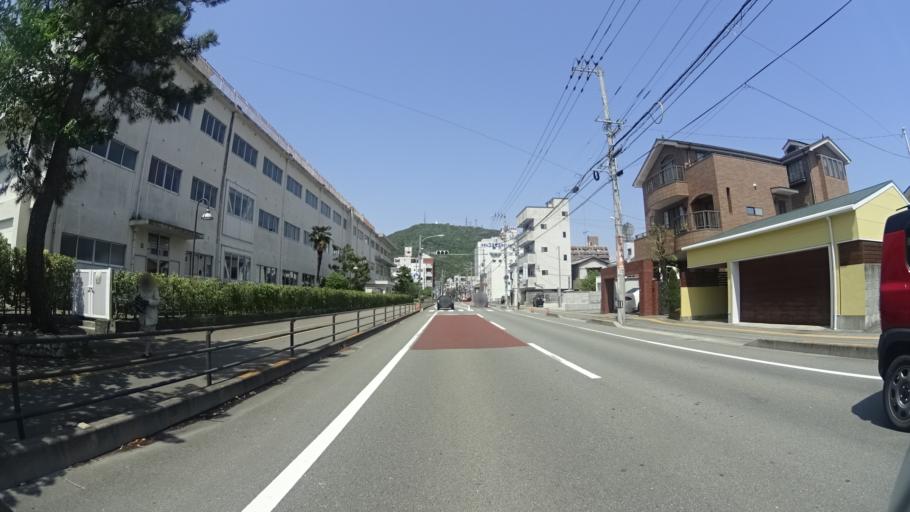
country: JP
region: Tokushima
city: Tokushima-shi
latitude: 34.0623
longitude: 134.5543
